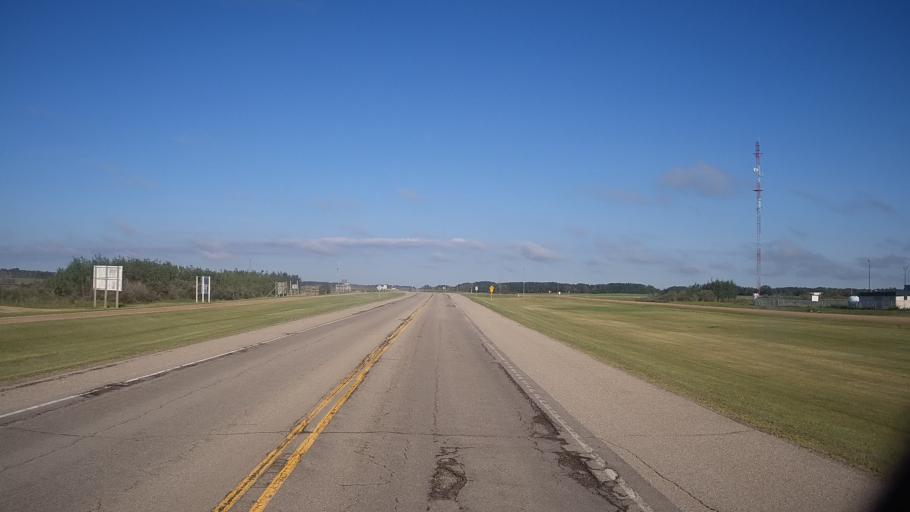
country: CA
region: Saskatchewan
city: Lanigan
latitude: 51.8483
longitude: -105.0476
